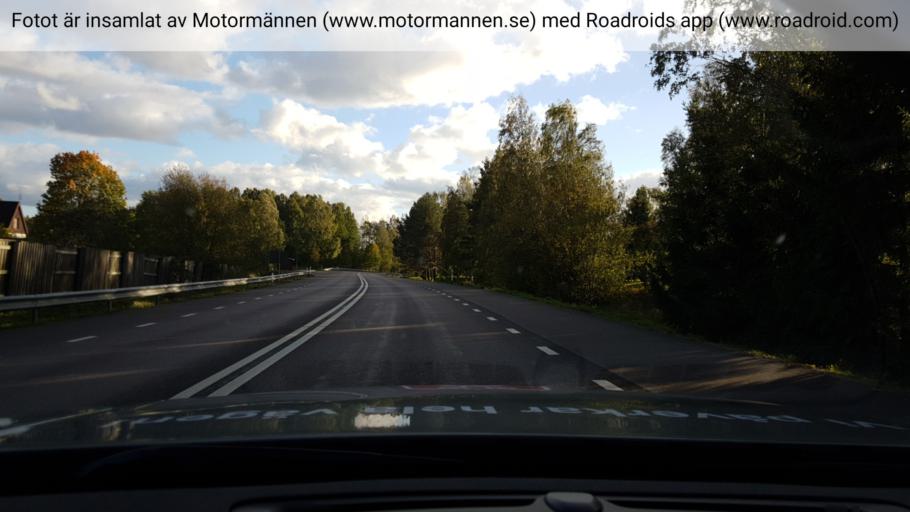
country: SE
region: Vaermland
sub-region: Karlstads Kommun
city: Molkom
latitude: 59.6019
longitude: 13.7380
